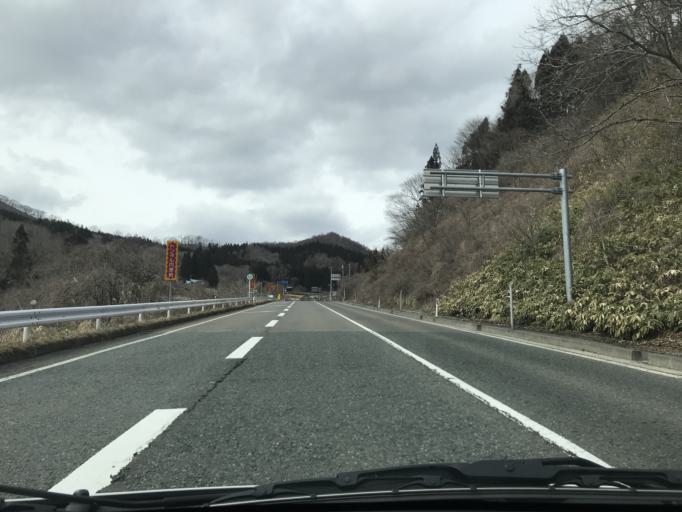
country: JP
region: Iwate
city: Tono
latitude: 39.3492
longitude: 141.4302
